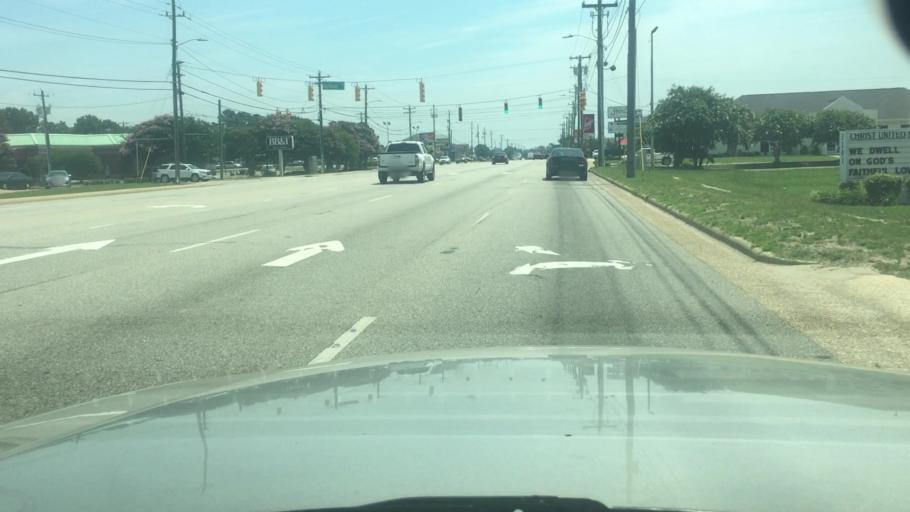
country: US
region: North Carolina
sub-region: Cumberland County
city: Fayetteville
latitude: 35.0447
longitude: -78.9312
